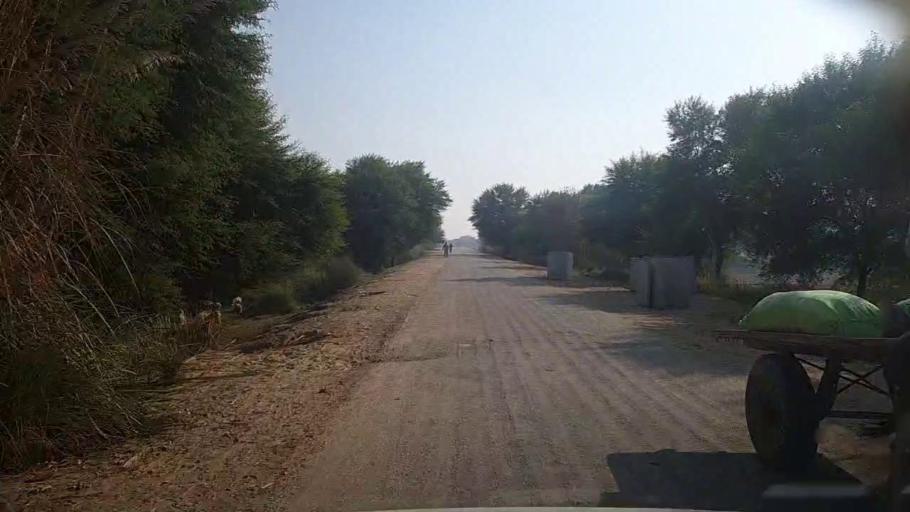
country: PK
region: Sindh
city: Kandiari
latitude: 26.8372
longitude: 68.4891
